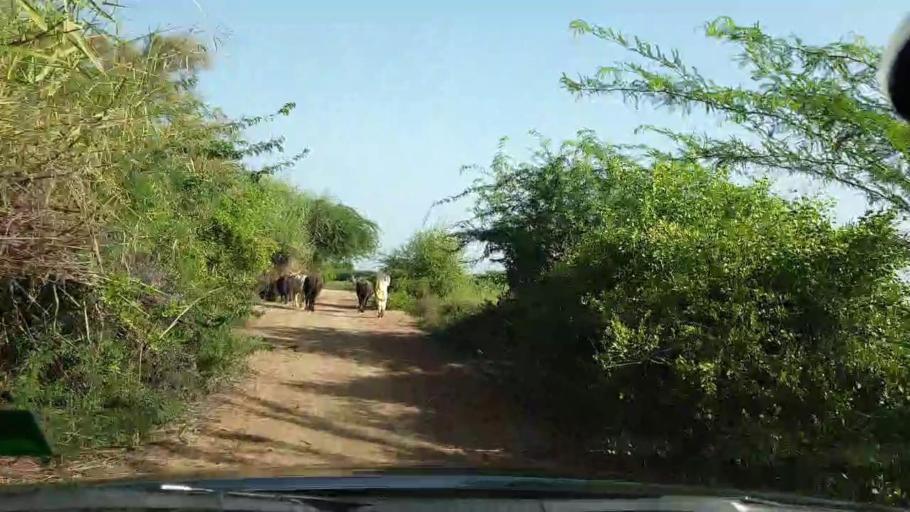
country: PK
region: Sindh
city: Tando Bago
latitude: 24.6633
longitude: 69.0429
